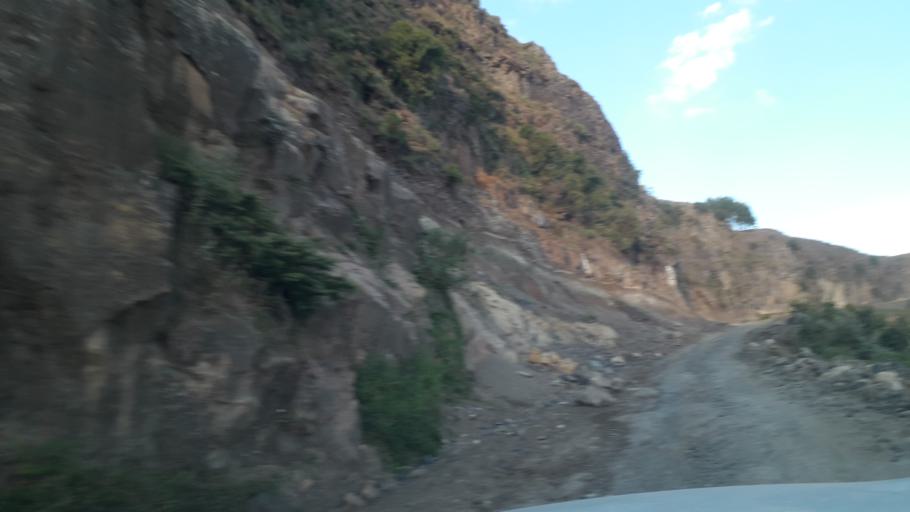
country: ET
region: Amhara
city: Lalibela
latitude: 11.5532
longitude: 39.2166
